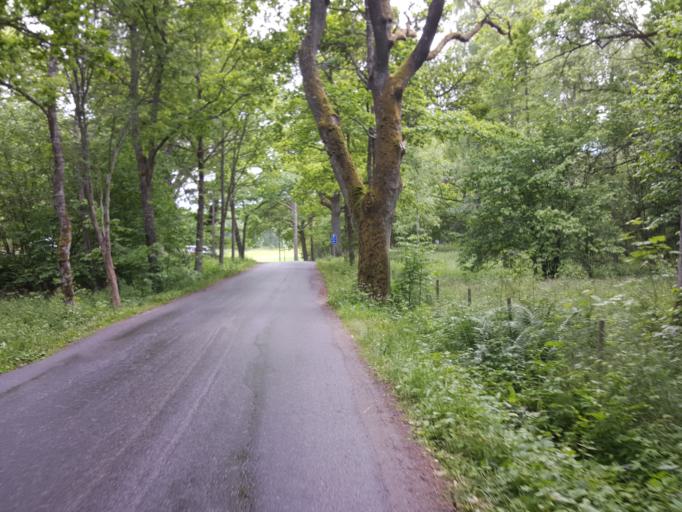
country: SE
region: Stockholm
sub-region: Nynashamns Kommun
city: Osmo
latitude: 59.0491
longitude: 18.0161
